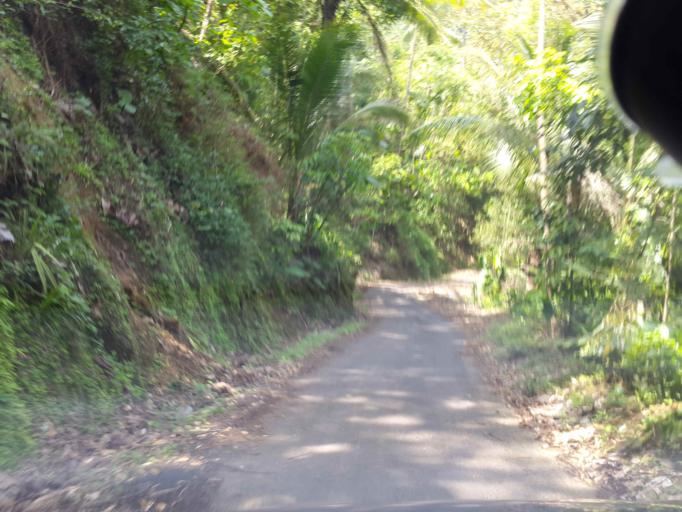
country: ID
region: Central Java
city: Kutoarjo
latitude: -7.7565
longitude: 110.0748
